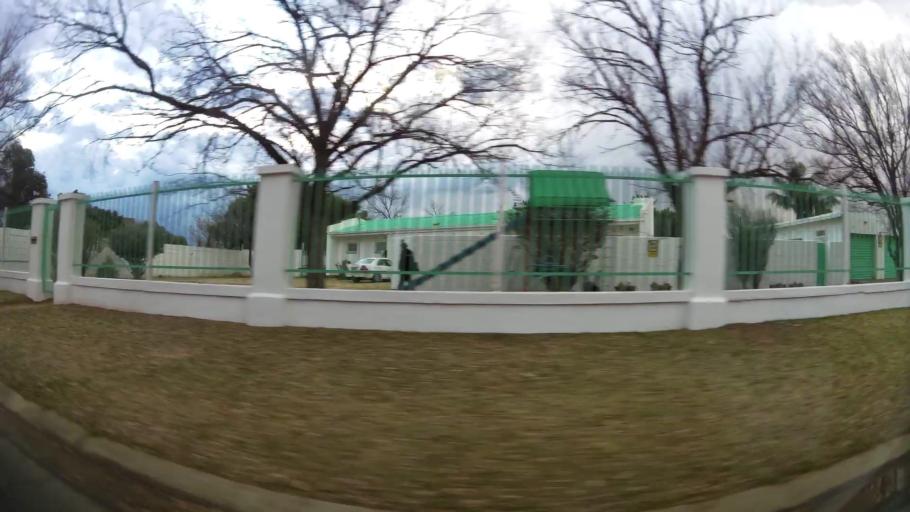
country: ZA
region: Orange Free State
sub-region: Lejweleputswa District Municipality
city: Welkom
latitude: -27.9564
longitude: 26.7373
